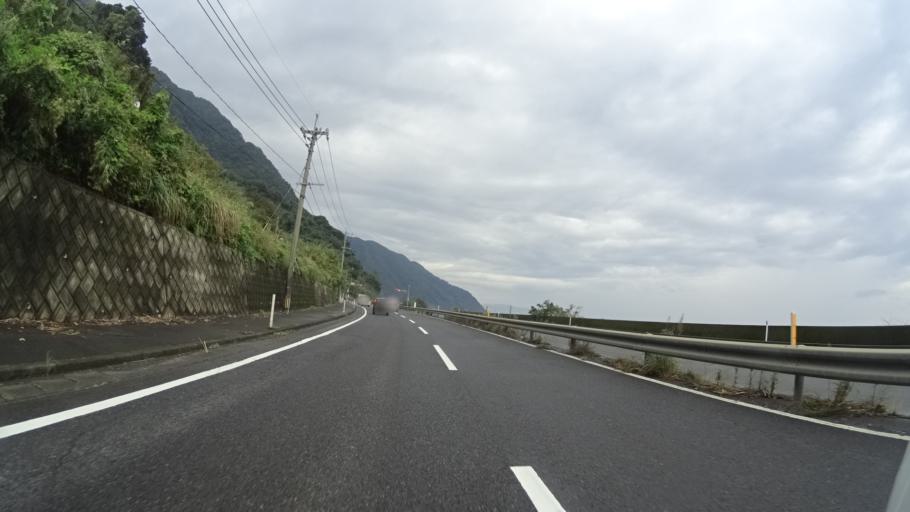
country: JP
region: Kagoshima
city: Kajiki
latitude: 31.6664
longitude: 130.6127
